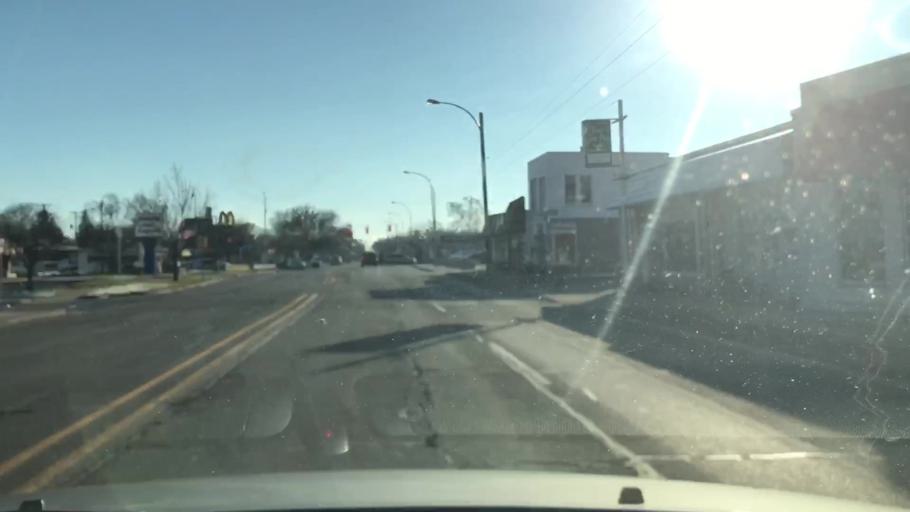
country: US
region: Michigan
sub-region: Oakland County
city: Clawson
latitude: 42.5204
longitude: -83.1392
